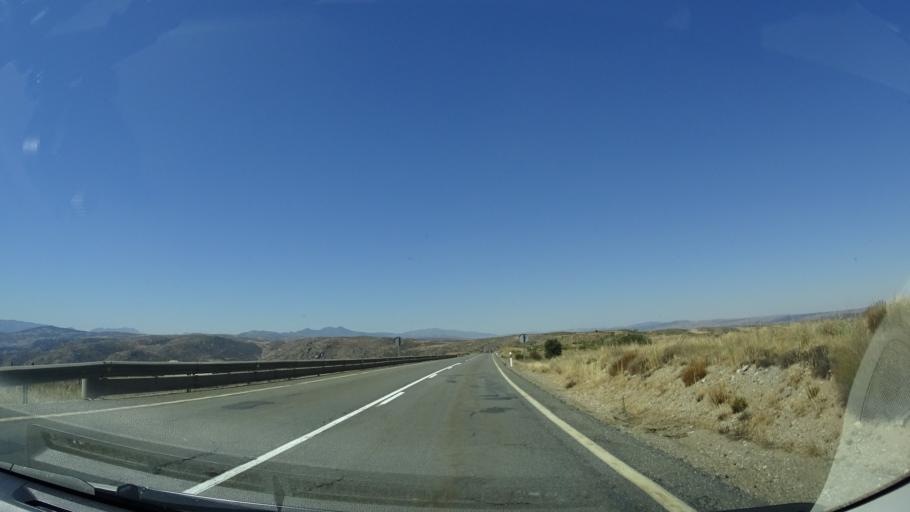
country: ES
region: Castille and Leon
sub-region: Provincia de Avila
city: Santa Cruz de Pinares
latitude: 40.6075
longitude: -4.5406
